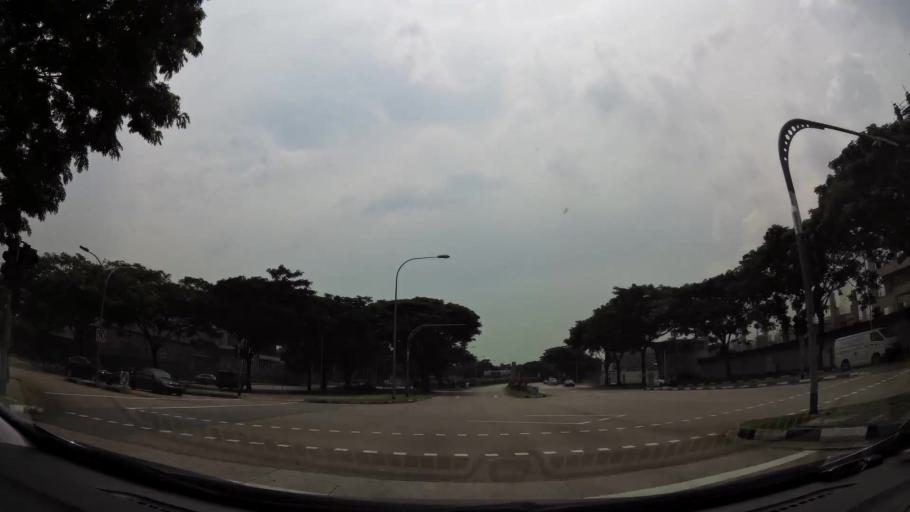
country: SG
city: Singapore
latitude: 1.3442
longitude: 103.8992
